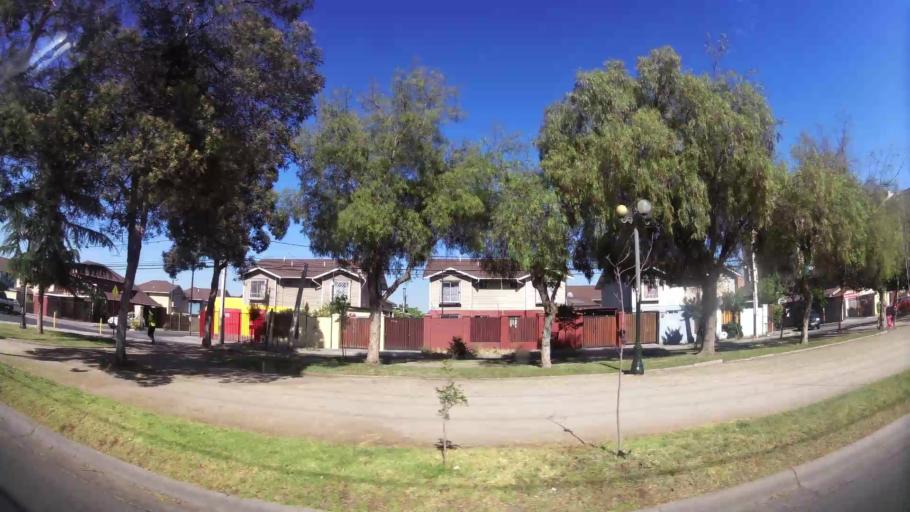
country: CL
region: Santiago Metropolitan
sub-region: Provincia de Maipo
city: San Bernardo
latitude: -33.6081
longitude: -70.6944
